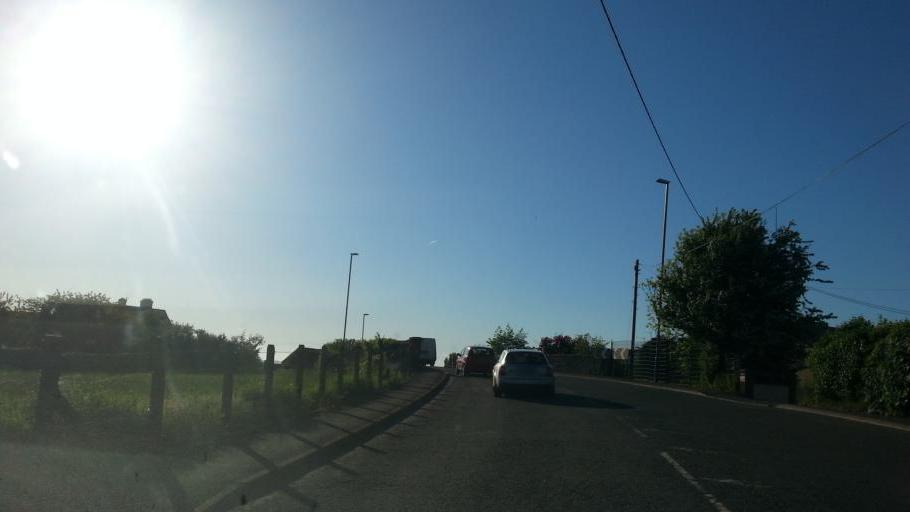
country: GB
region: England
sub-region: Bath and North East Somerset
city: Whitchurch
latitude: 51.4040
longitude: -2.5556
